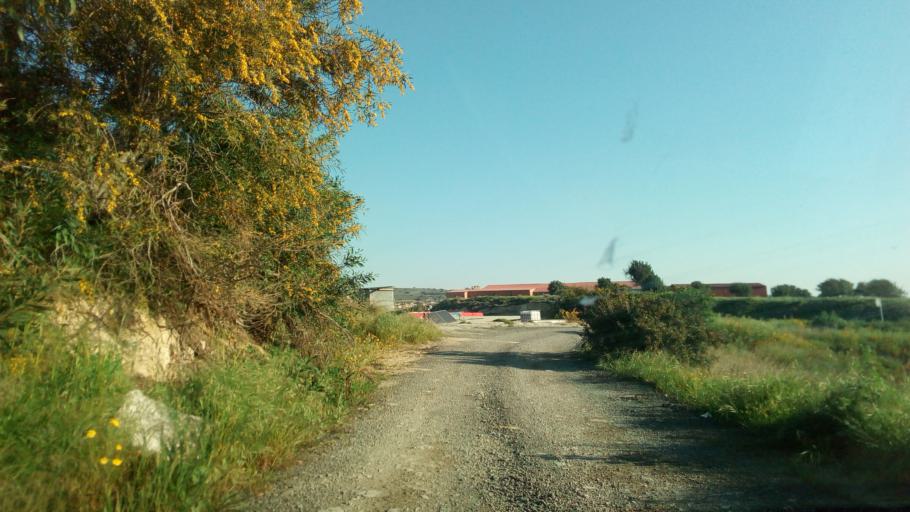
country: CY
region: Larnaka
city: Kofinou
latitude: 34.8454
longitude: 33.4498
